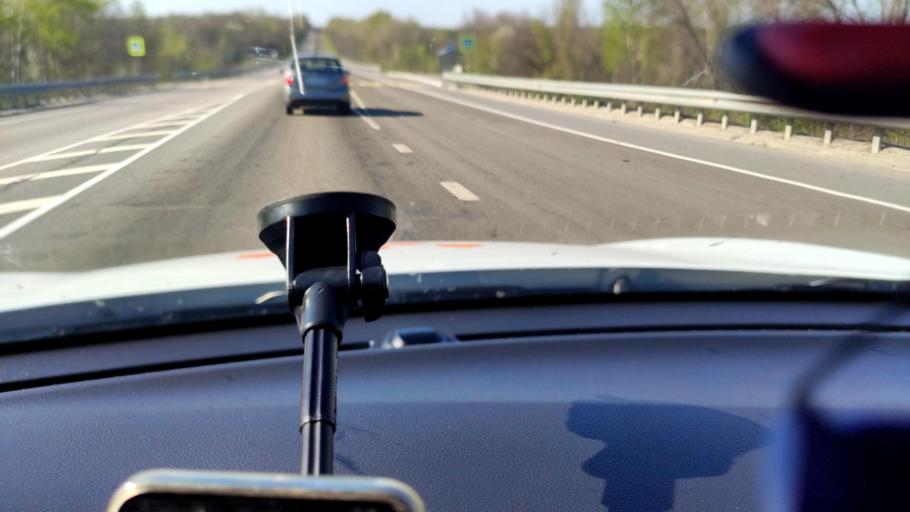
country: RU
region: Voronezj
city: Uryv-Pokrovka
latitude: 51.2051
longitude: 39.0773
